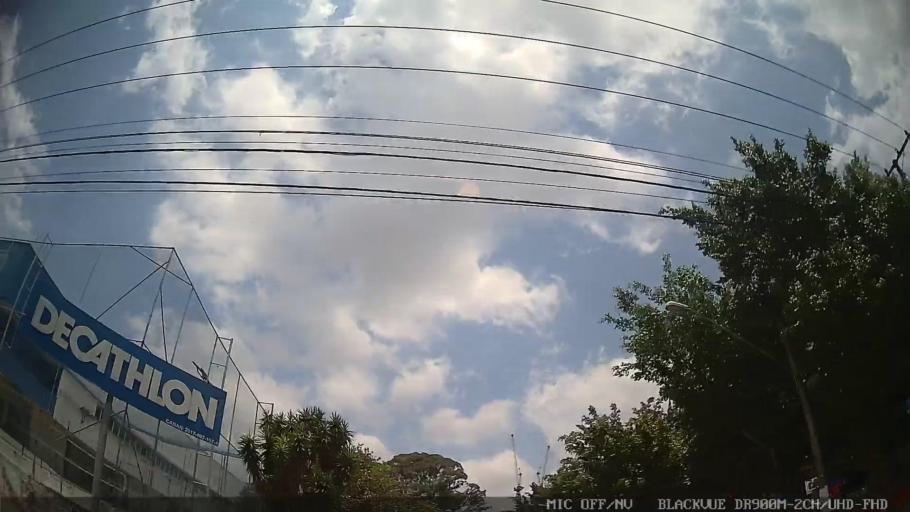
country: BR
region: Sao Paulo
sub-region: Sao Paulo
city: Sao Paulo
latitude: -23.5152
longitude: -46.6746
